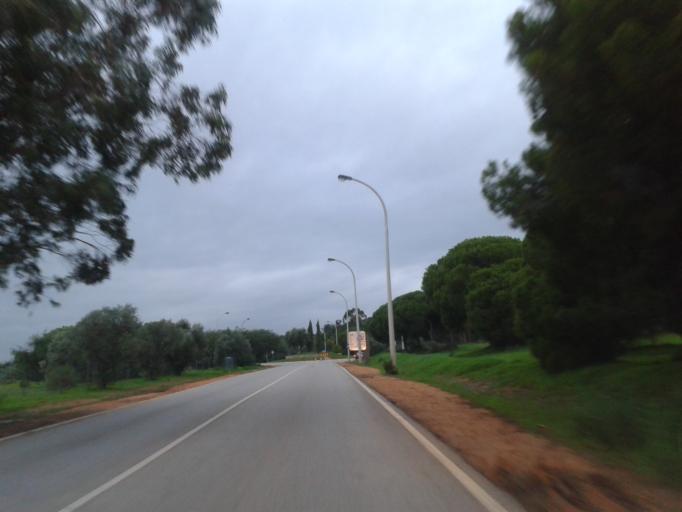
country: PT
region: Faro
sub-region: Loule
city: Boliqueime
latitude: 37.1099
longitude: -8.1409
